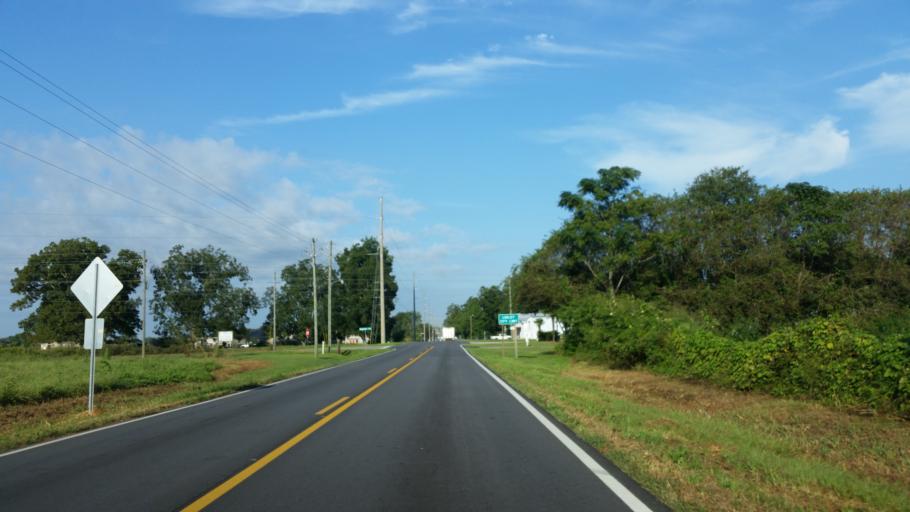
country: US
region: Alabama
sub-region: Baldwin County
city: Loxley
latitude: 30.6184
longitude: -87.7459
